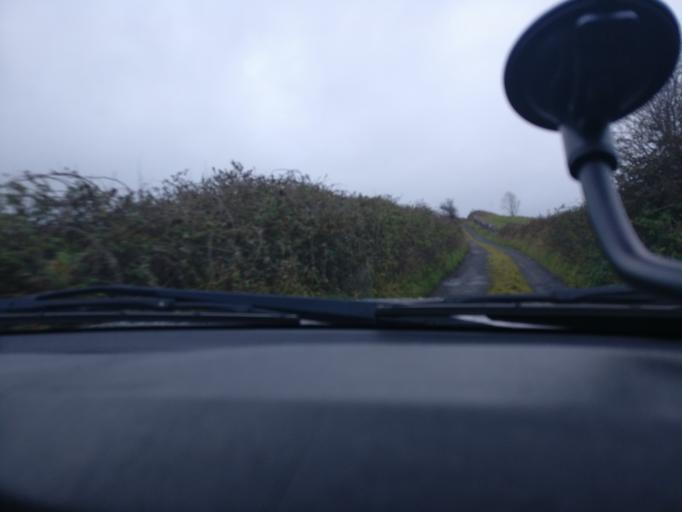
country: IE
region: Connaught
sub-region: County Galway
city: Loughrea
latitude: 53.2113
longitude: -8.5458
